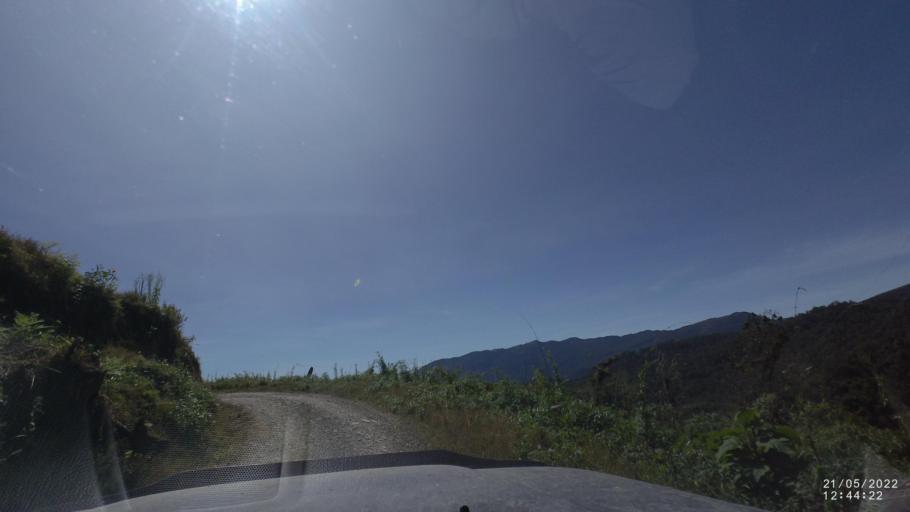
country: BO
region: Cochabamba
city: Colomi
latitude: -17.1896
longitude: -65.9339
